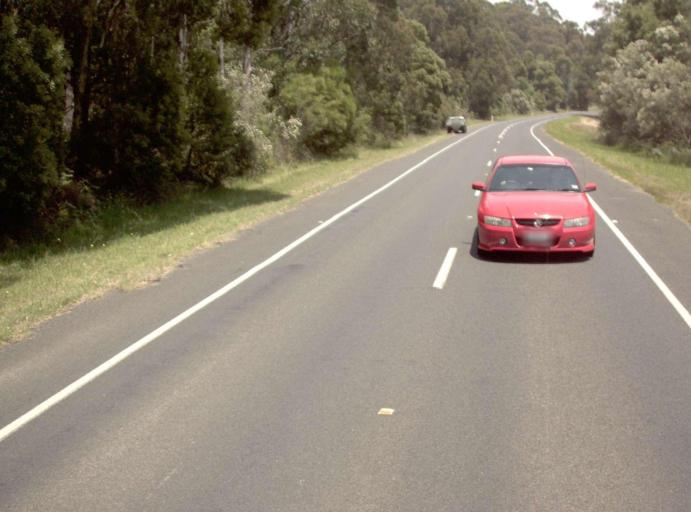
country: AU
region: Victoria
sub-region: Latrobe
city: Traralgon
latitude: -38.3592
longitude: 146.7456
